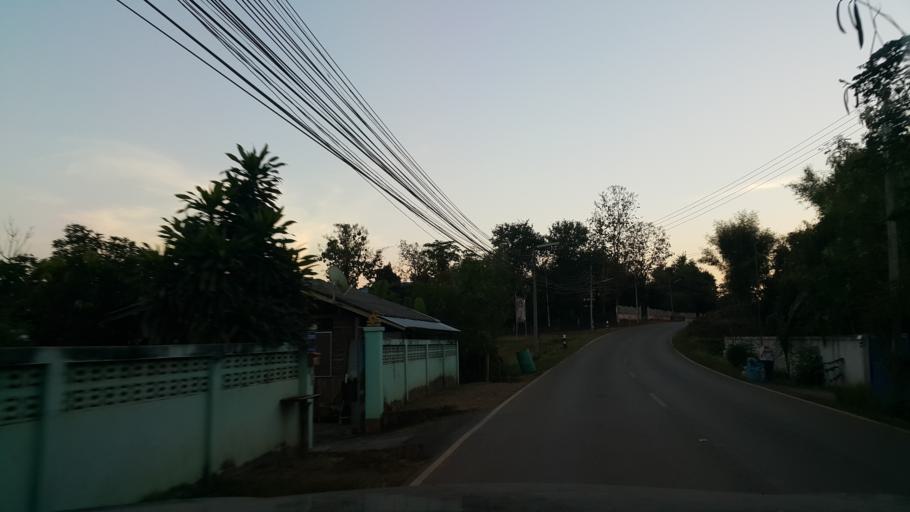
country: TH
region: Uttaradit
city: Uttaradit
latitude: 17.6582
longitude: 100.0933
